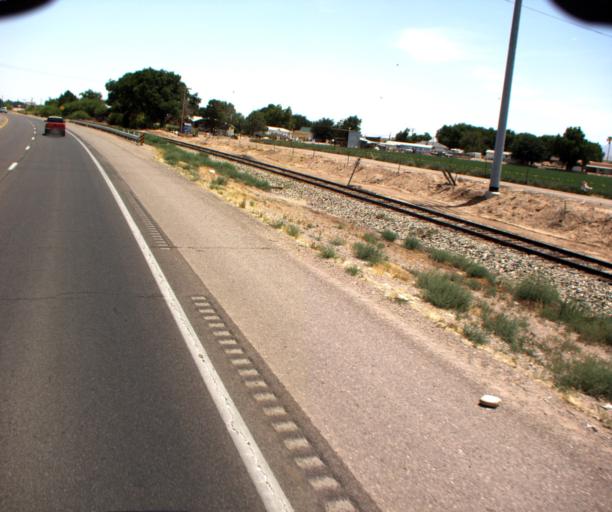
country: US
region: Arizona
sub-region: Graham County
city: Thatcher
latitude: 32.8517
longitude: -109.7766
